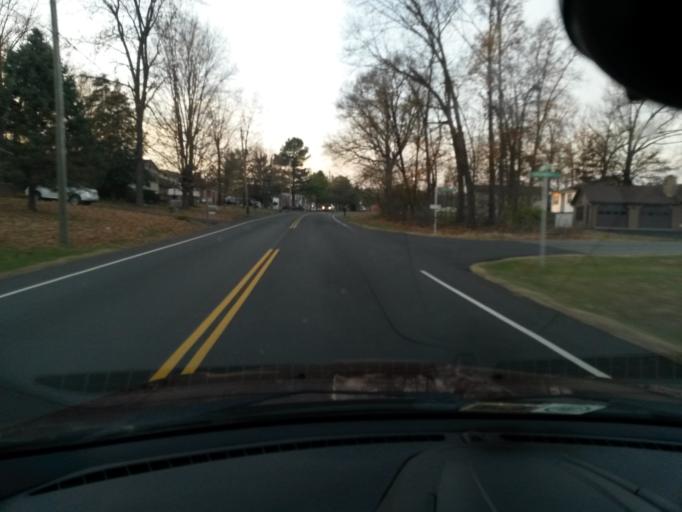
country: US
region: Virginia
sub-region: Roanoke County
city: Hollins
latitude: 37.3342
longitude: -79.9400
